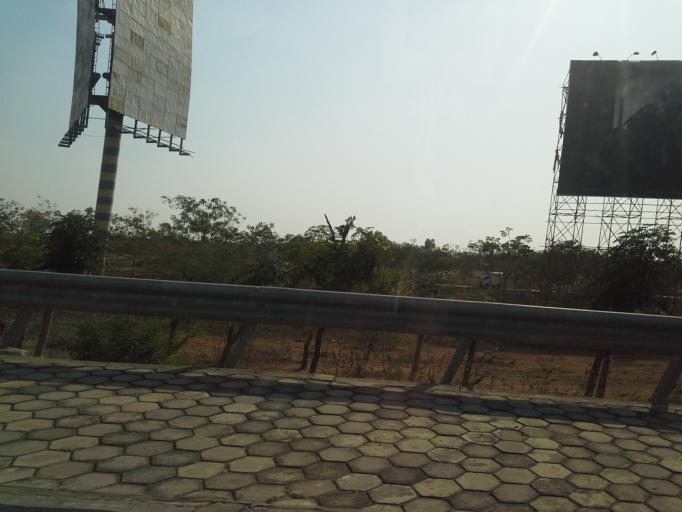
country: IN
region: Telangana
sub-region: Rangareddi
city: Balapur
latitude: 17.2440
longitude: 78.3862
